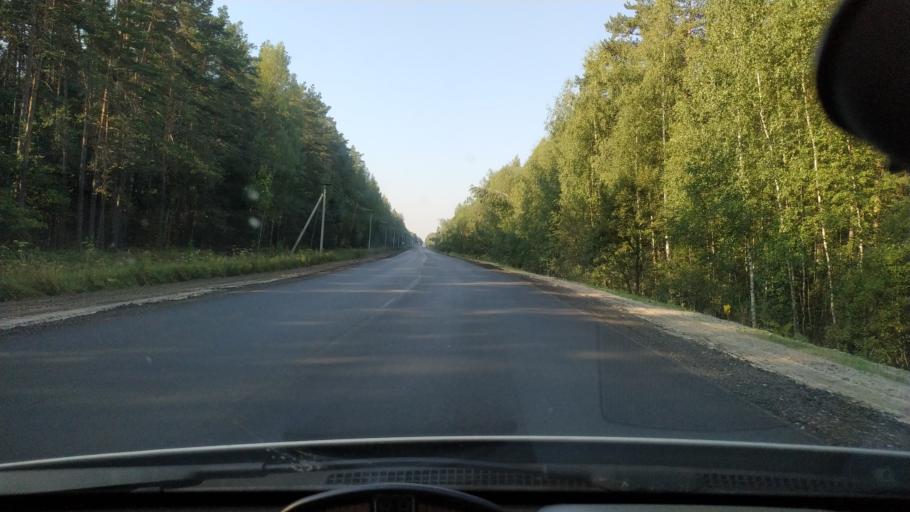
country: RU
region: Moskovskaya
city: Misheronskiy
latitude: 55.6244
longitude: 39.7335
